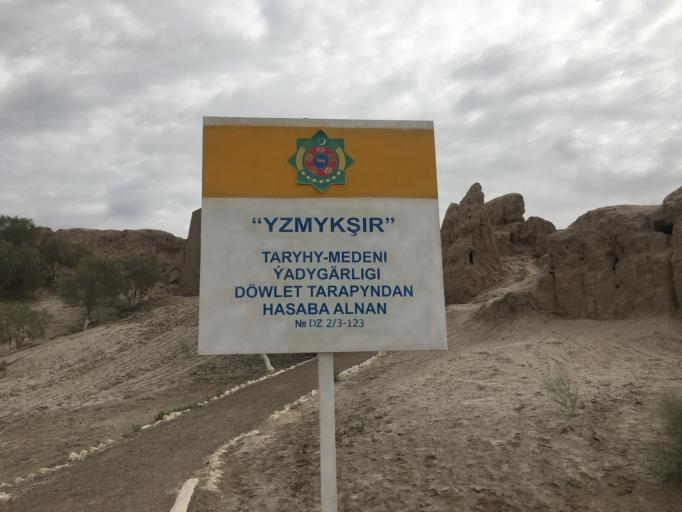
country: TM
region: Dasoguz
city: Yylanly
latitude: 41.7289
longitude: 59.7180
